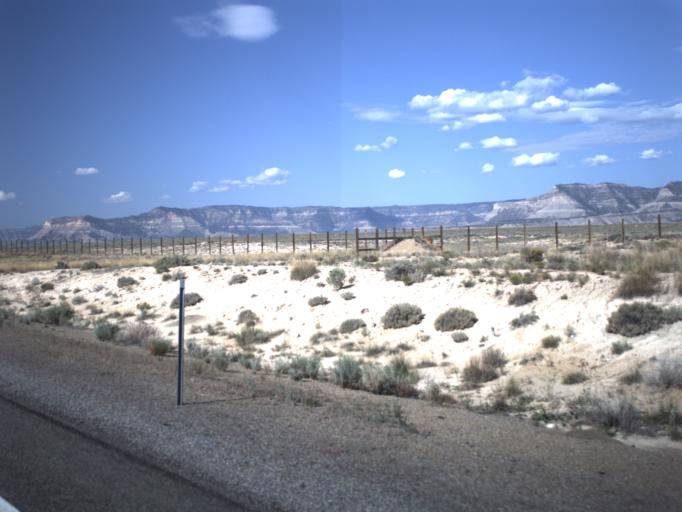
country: US
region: Utah
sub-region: Emery County
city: Huntington
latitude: 39.4036
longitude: -110.8881
